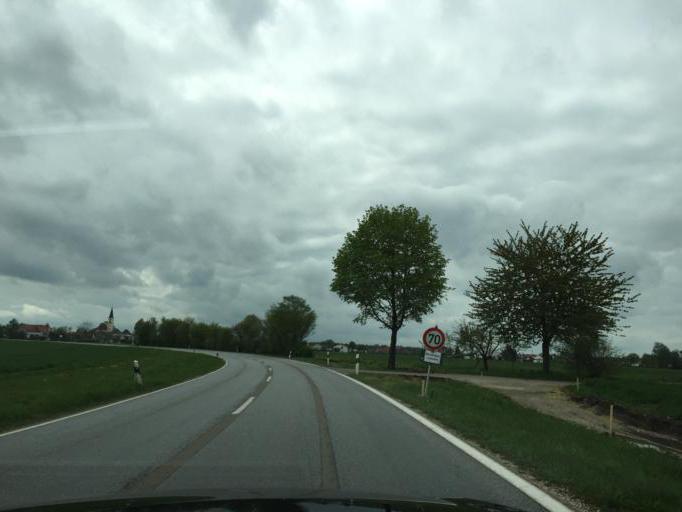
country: DE
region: Bavaria
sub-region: Swabia
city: Binswangen
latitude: 48.5711
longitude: 10.6061
